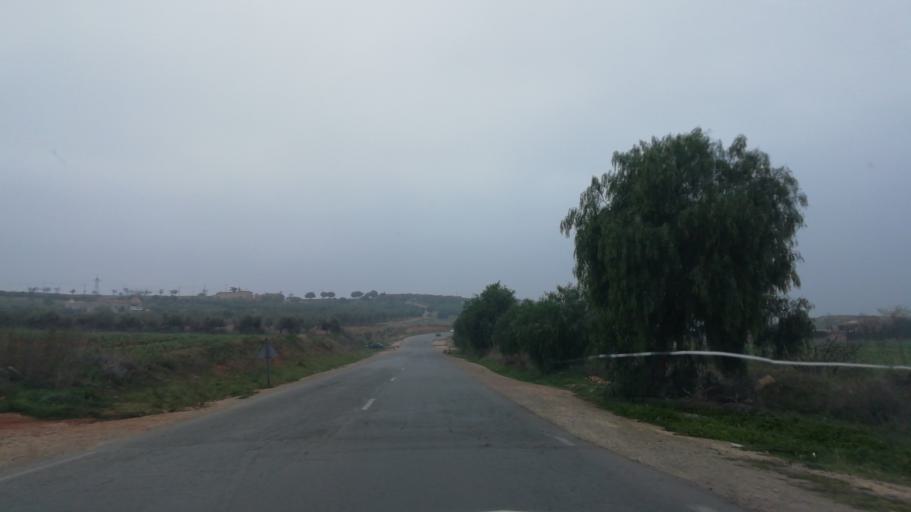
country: DZ
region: Mascara
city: Mascara
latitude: 35.3896
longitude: 0.1613
